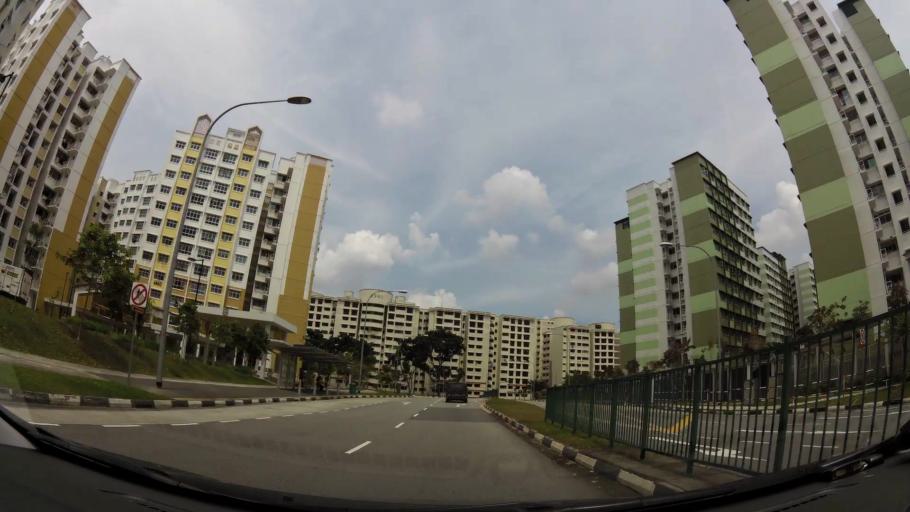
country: MY
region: Johor
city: Johor Bahru
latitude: 1.3752
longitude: 103.7420
